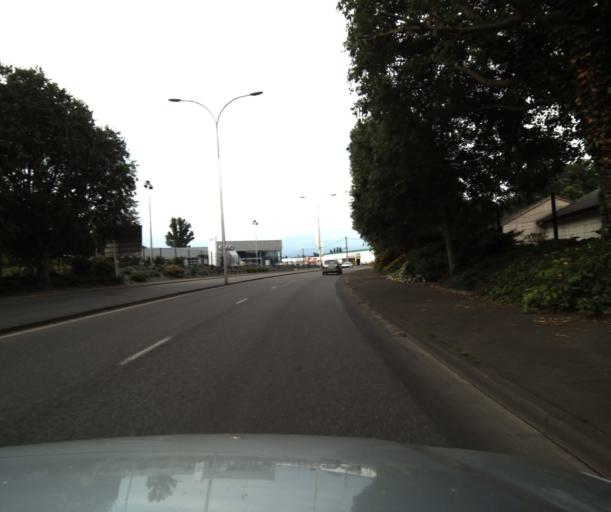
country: FR
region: Midi-Pyrenees
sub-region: Departement des Hautes-Pyrenees
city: Tarbes
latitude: 43.2215
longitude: 0.0918
